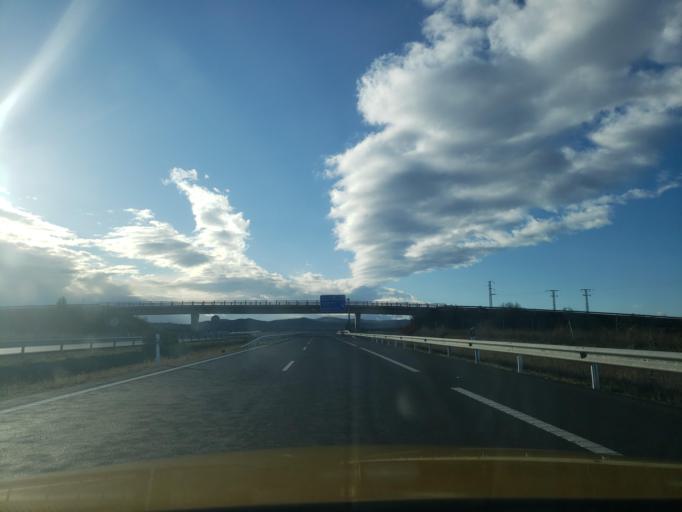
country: ES
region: Castille-La Mancha
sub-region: Province of Toledo
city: Consuegra
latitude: 39.4768
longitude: -3.6113
